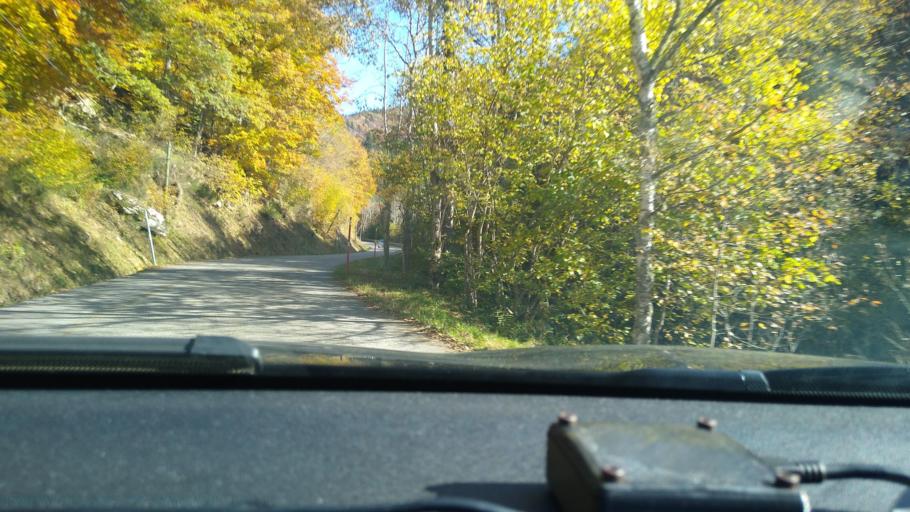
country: FR
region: Midi-Pyrenees
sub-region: Departement de l'Ariege
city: Ax-les-Thermes
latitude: 42.7170
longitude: 1.9194
